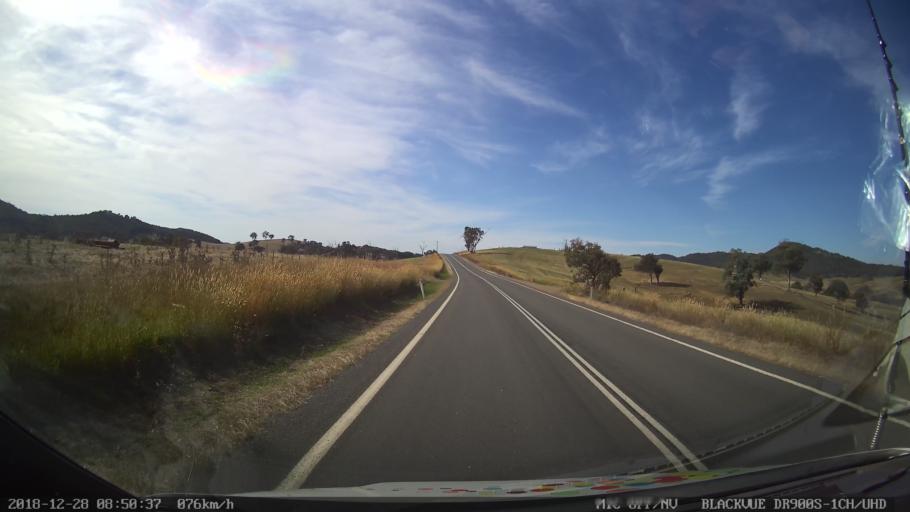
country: AU
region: New South Wales
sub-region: Upper Lachlan Shire
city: Crookwell
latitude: -34.0593
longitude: 149.3379
